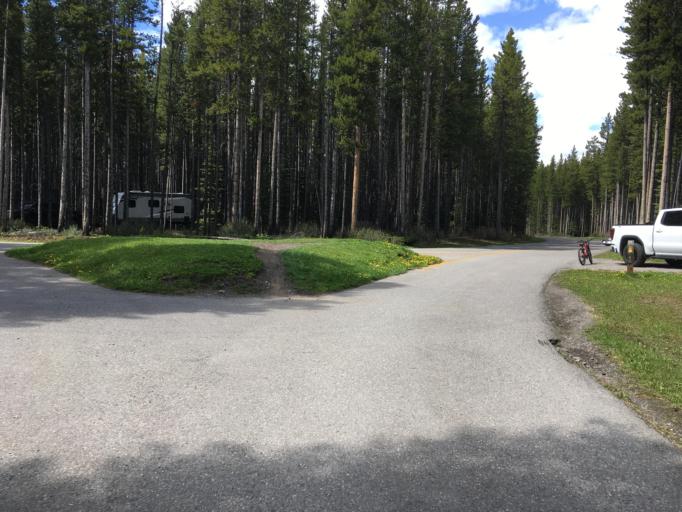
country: CA
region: Alberta
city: Canmore
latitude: 50.6278
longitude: -115.0997
